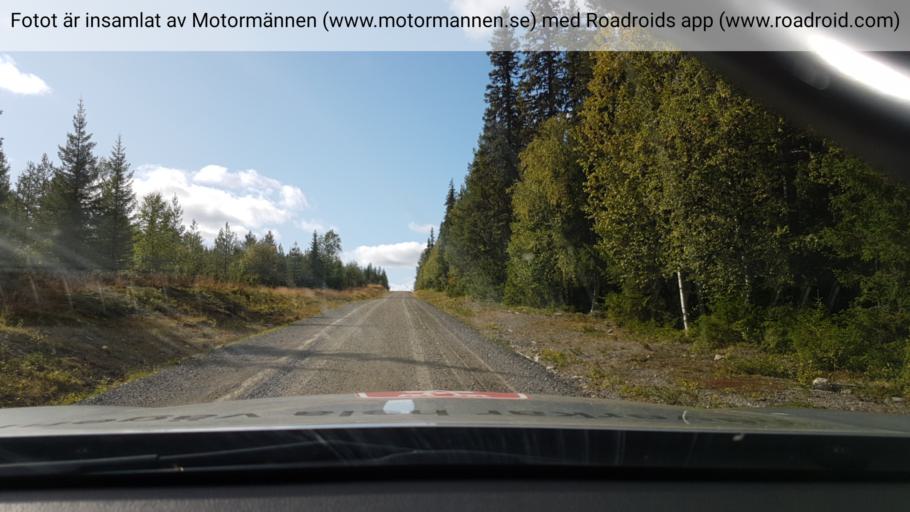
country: SE
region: Vaesterbotten
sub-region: Mala Kommun
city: Mala
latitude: 65.4672
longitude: 18.1790
